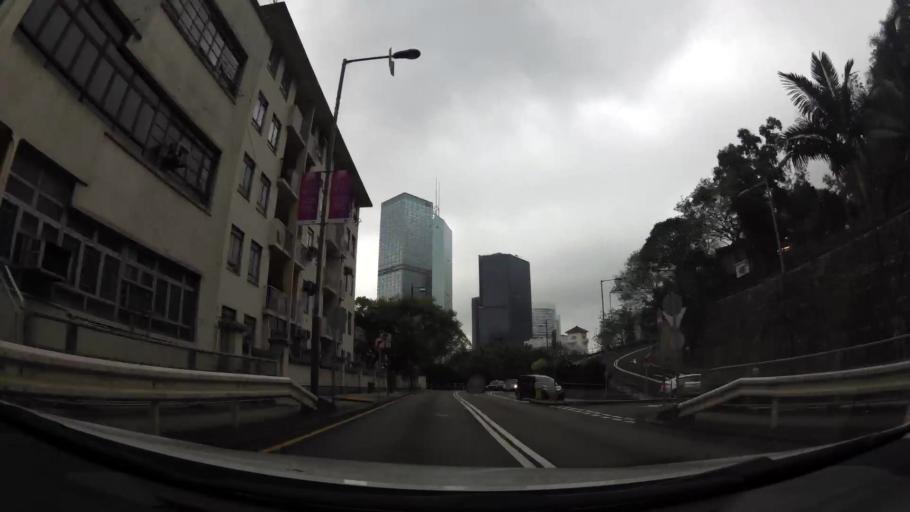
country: HK
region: Central and Western
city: Central
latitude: 22.2793
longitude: 114.1555
